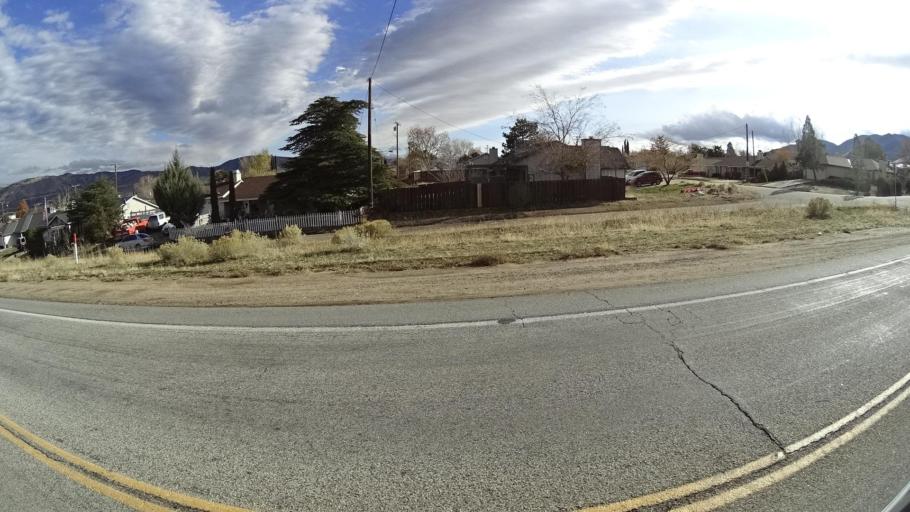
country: US
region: California
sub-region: Kern County
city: Golden Hills
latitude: 35.1280
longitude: -118.4949
